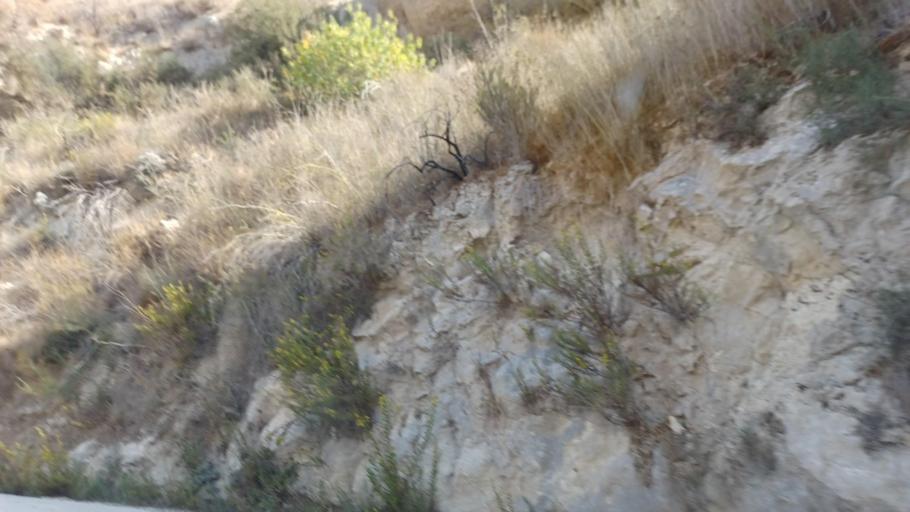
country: CY
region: Pafos
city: Tala
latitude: 34.9094
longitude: 32.4592
